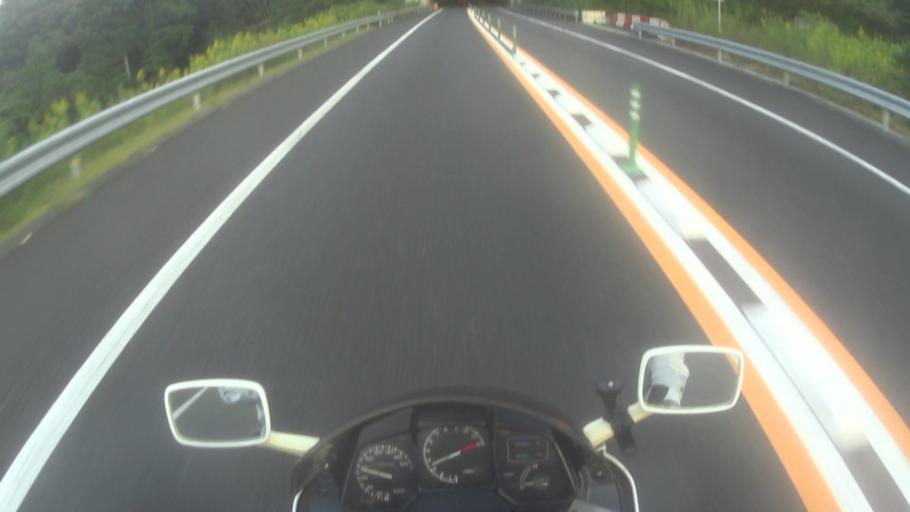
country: JP
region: Kyoto
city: Miyazu
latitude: 35.5475
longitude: 135.1496
